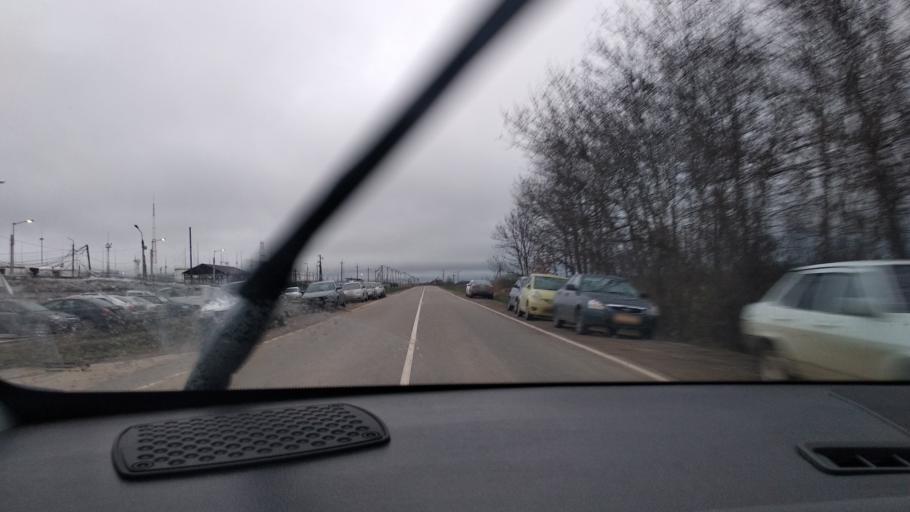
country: RU
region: Krasnodarskiy
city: Afipskiy
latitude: 44.8920
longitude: 38.8051
